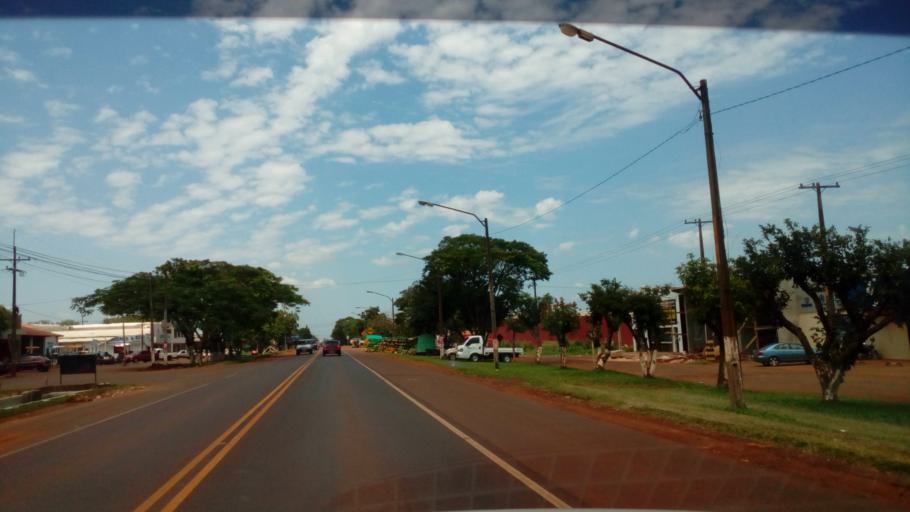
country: PY
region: Alto Parana
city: Santa Rita
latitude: -25.7800
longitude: -55.0772
